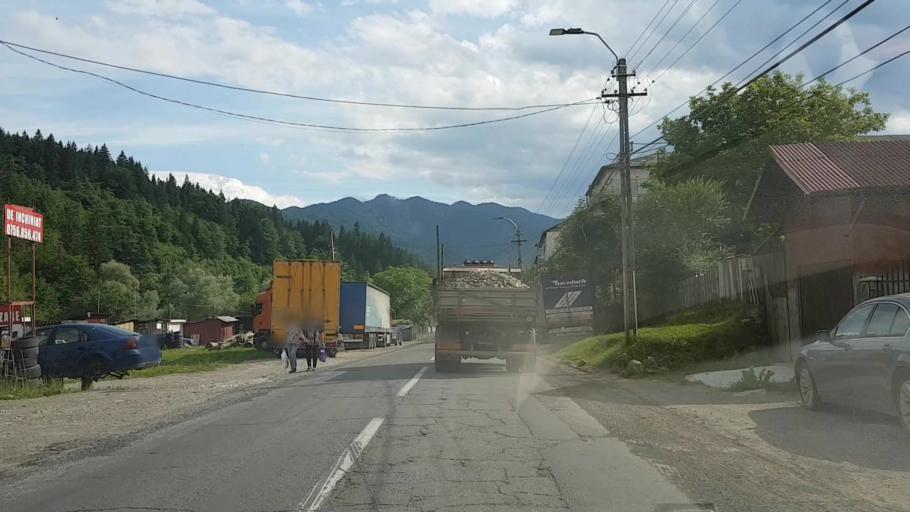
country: RO
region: Neamt
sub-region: Comuna Bicaz
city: Dodeni
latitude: 46.9276
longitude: 26.0947
